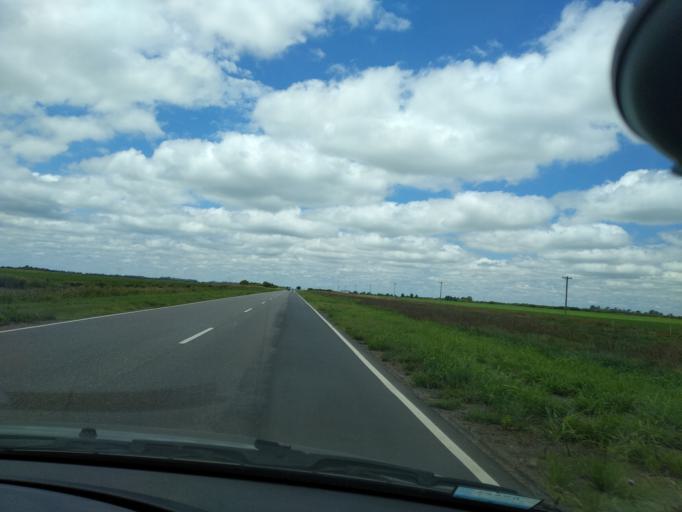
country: AR
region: Cordoba
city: Toledo
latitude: -31.6450
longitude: -64.0089
